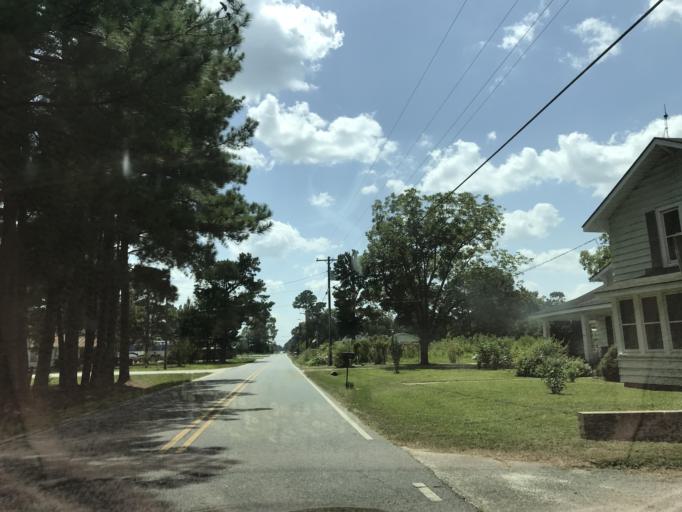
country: US
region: North Carolina
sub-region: Sampson County
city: Plain View
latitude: 35.2440
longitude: -78.3599
